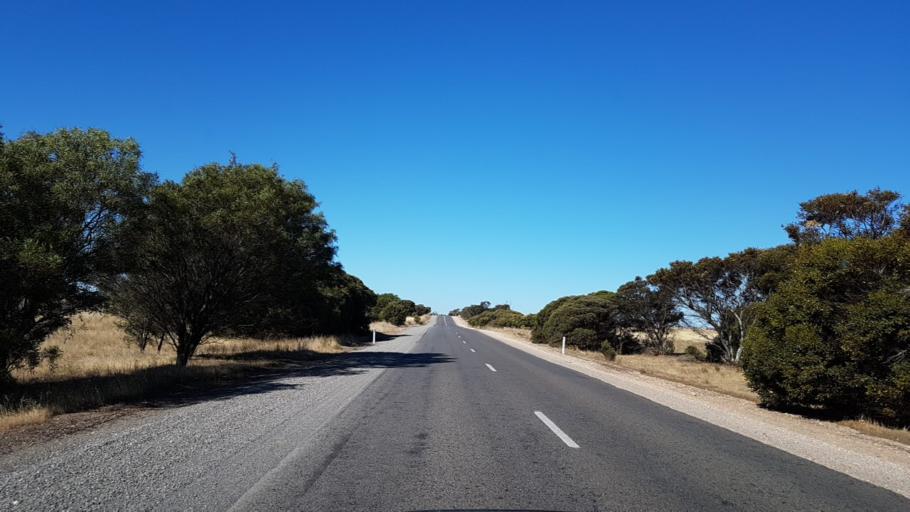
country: AU
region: South Australia
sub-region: Yorke Peninsula
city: Honiton
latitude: -34.8786
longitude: 137.4777
